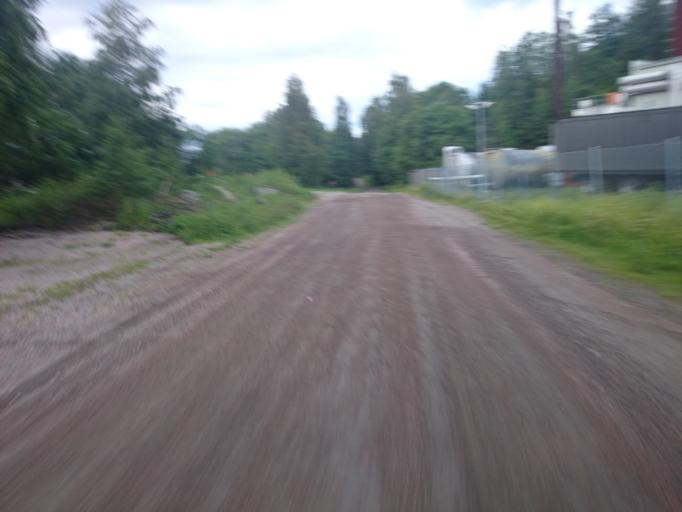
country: SE
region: Vaesternorrland
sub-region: Sundsvalls Kommun
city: Kvissleby
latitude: 62.3066
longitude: 17.3754
